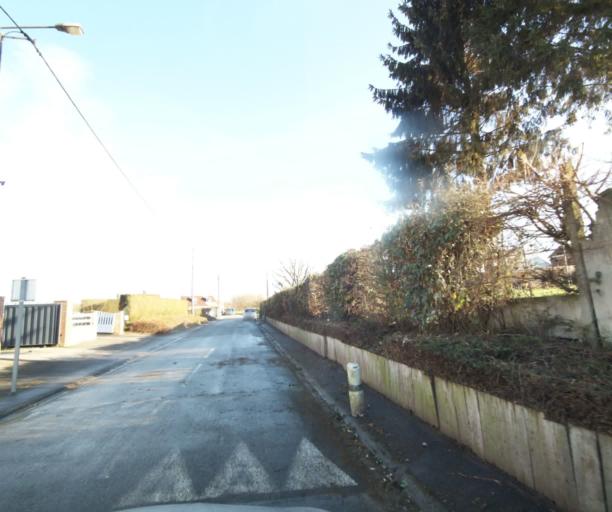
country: FR
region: Nord-Pas-de-Calais
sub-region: Departement du Nord
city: Saultain
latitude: 50.3359
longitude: 3.5857
